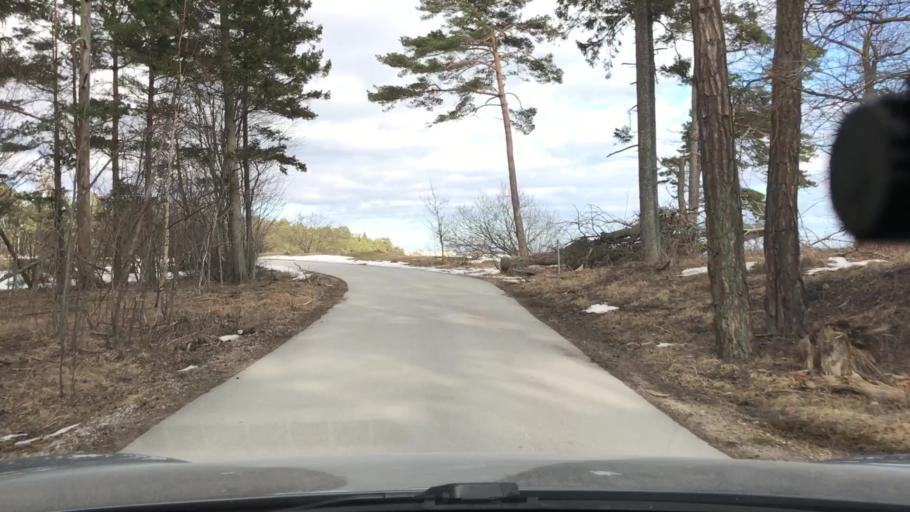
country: SE
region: Gotland
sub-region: Gotland
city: Slite
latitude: 57.3440
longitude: 18.7290
